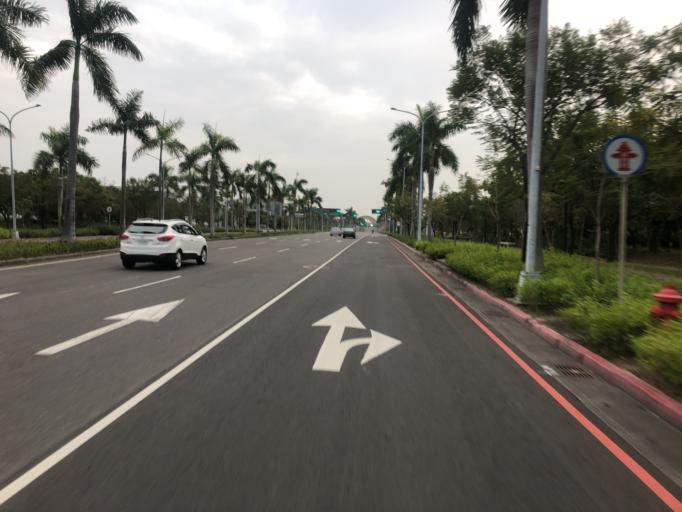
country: TW
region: Taiwan
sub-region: Tainan
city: Tainan
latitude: 23.0972
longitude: 120.2812
